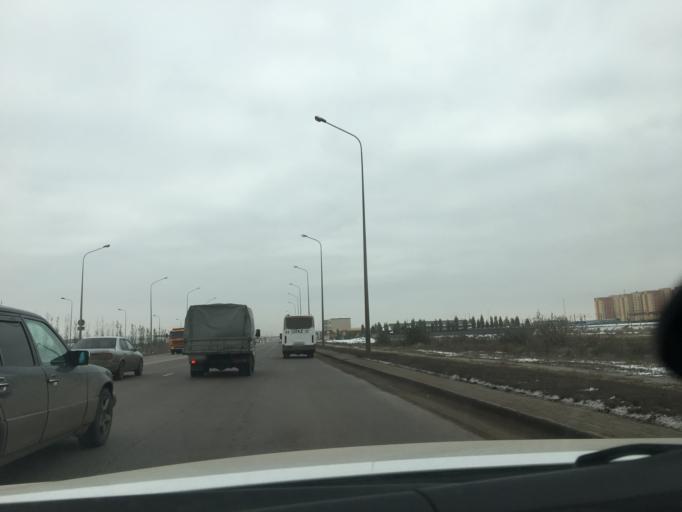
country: KZ
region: Astana Qalasy
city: Astana
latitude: 51.1609
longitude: 71.5172
